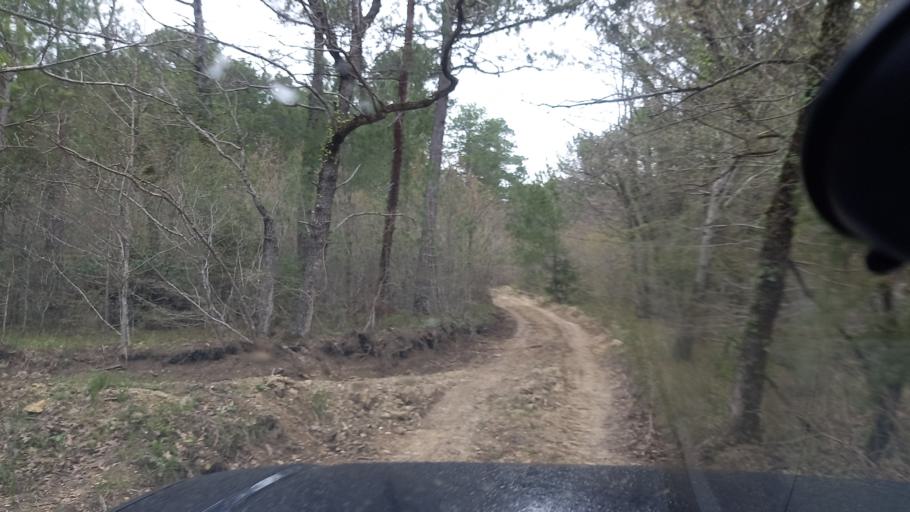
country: RU
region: Krasnodarskiy
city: Arkhipo-Osipovka
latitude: 44.3713
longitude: 38.4727
